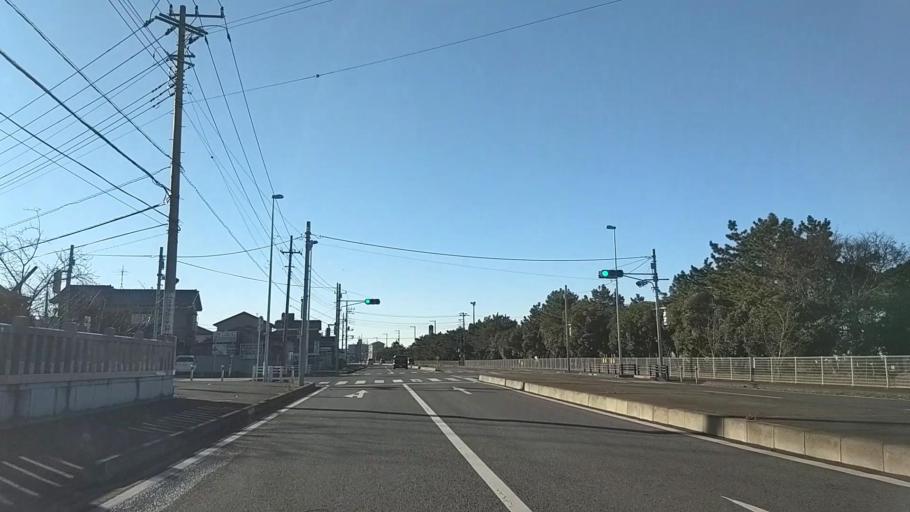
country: JP
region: Chiba
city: Kisarazu
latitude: 35.3911
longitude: 139.9196
